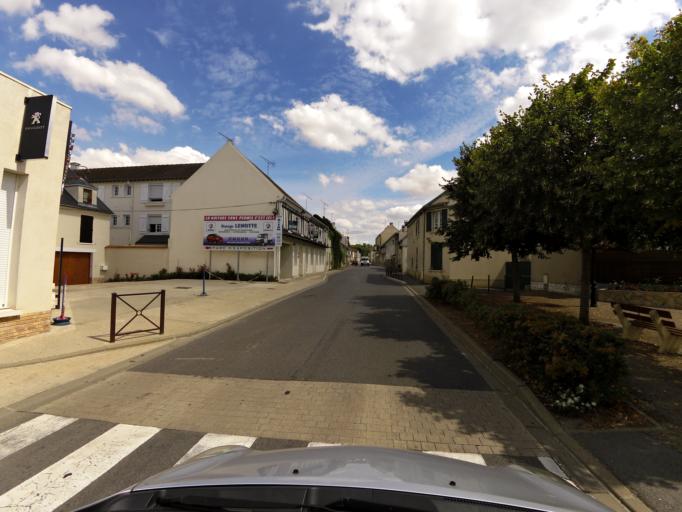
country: FR
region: Ile-de-France
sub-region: Departement de Seine-et-Marne
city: Varreddes
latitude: 49.0039
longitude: 2.9273
